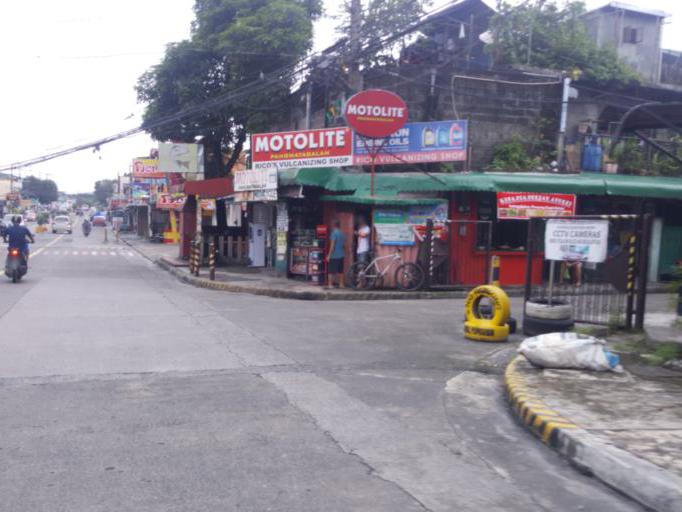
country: PH
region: Calabarzon
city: Bagong Pagasa
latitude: 14.7032
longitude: 121.0225
